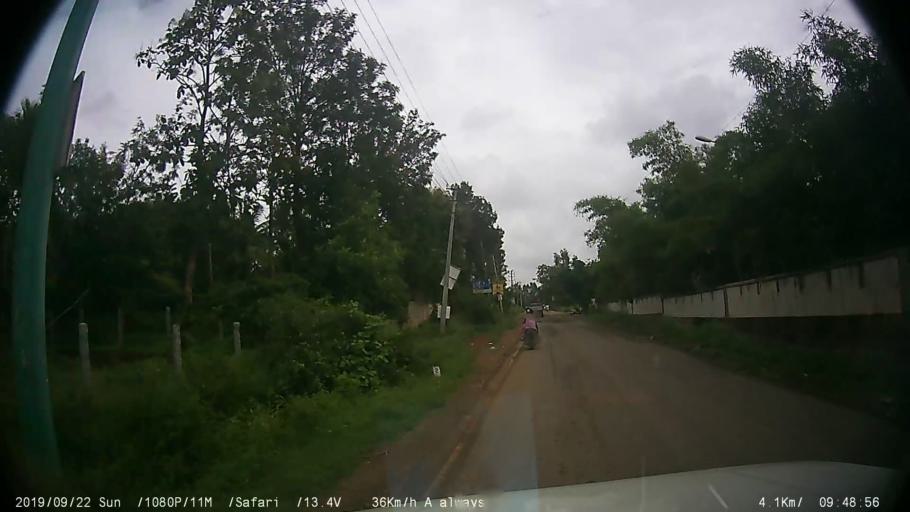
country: IN
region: Karnataka
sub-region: Bangalore Urban
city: Anekal
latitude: 12.8166
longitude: 77.6506
